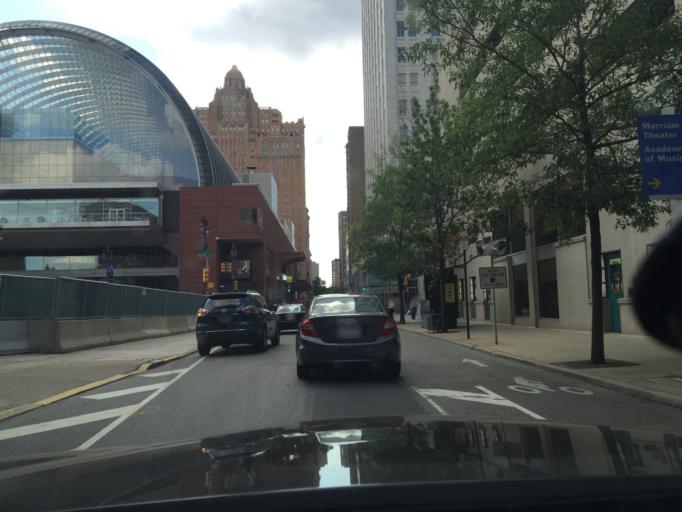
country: US
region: Pennsylvania
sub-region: Philadelphia County
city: Philadelphia
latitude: 39.9469
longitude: -75.1640
